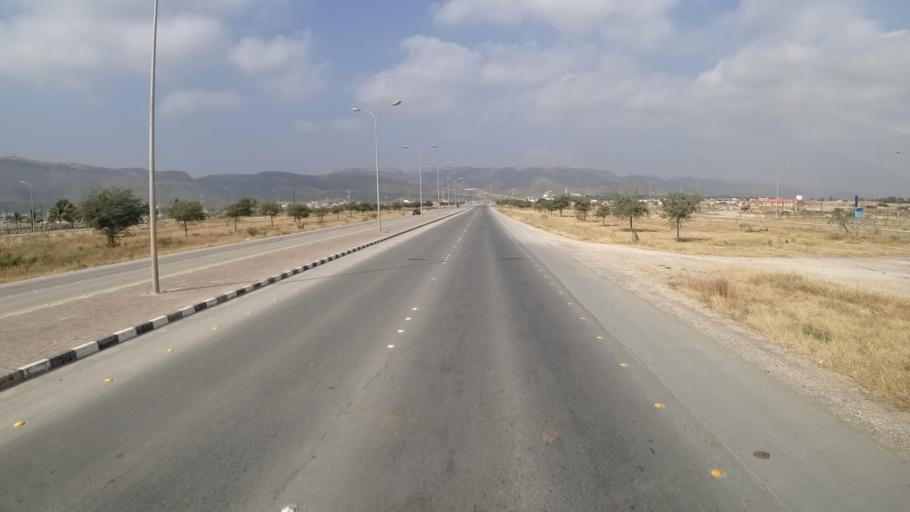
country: OM
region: Zufar
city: Salalah
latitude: 17.0739
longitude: 54.0669
